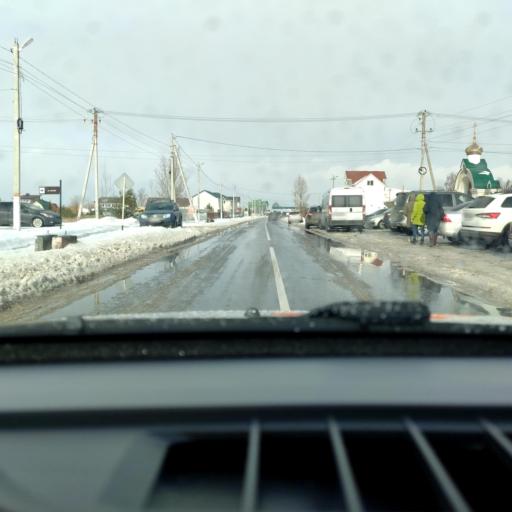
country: RU
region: Voronezj
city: Podgornoye
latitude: 51.7881
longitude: 39.1460
